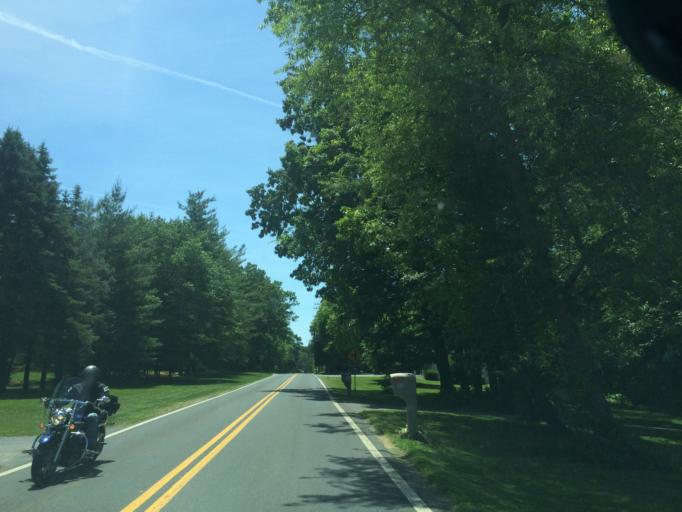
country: US
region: Maryland
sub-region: Carroll County
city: Sykesville
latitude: 39.3952
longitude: -77.0000
